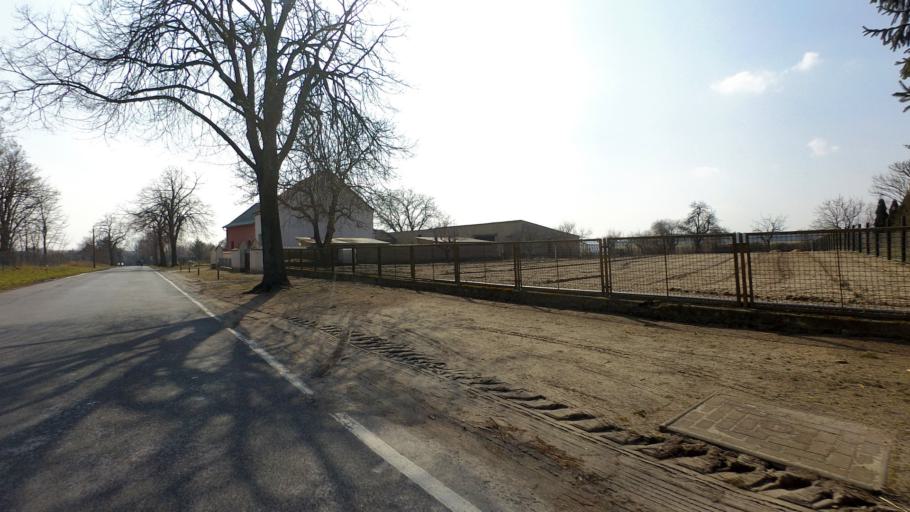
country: DE
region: Brandenburg
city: Gross Kreutz
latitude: 52.4211
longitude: 12.7912
